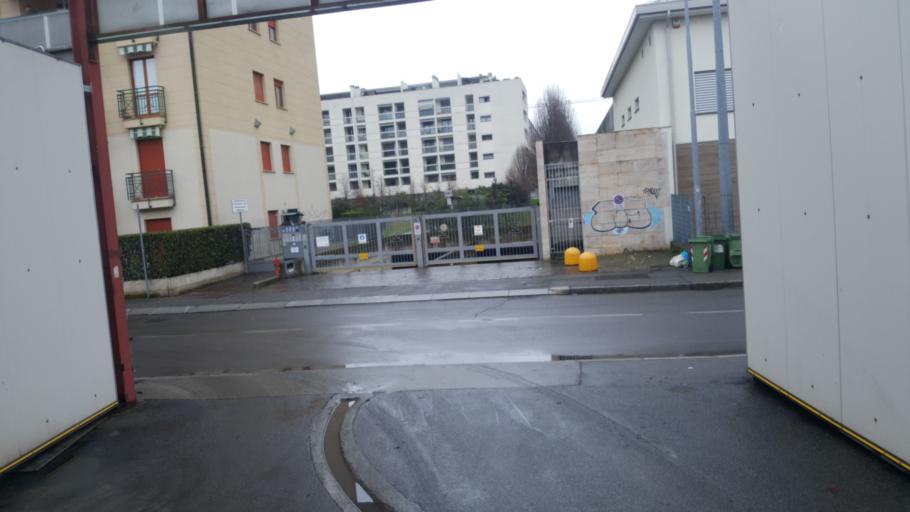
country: IT
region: Lombardy
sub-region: Provincia di Bergamo
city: Bergamo
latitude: 45.6974
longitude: 9.6865
